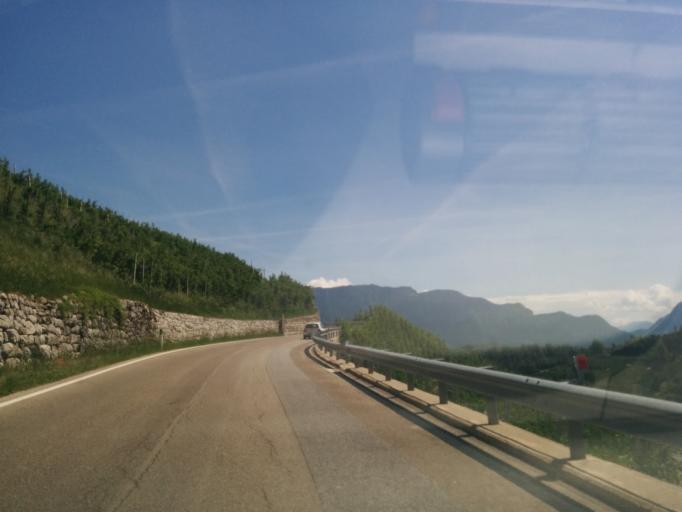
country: IT
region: Trentino-Alto Adige
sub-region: Provincia di Trento
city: Tuenno
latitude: 46.3205
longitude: 11.0188
